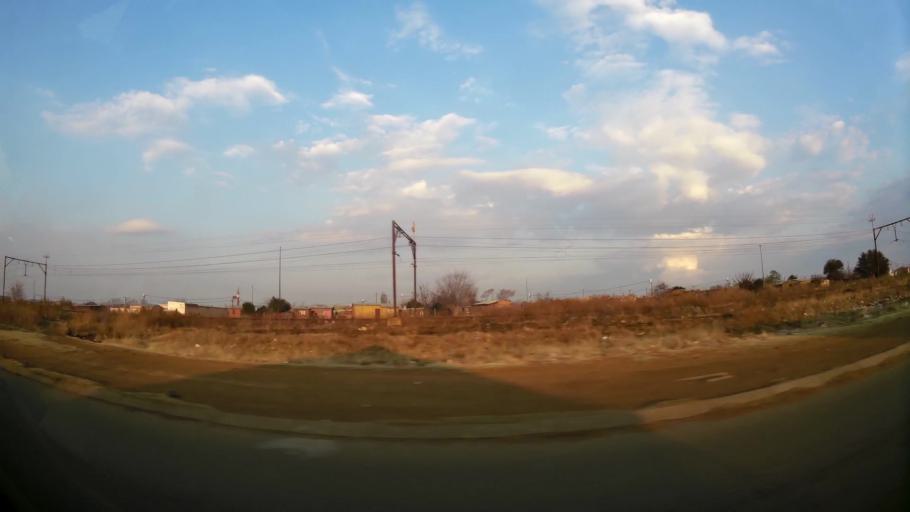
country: ZA
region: Gauteng
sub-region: City of Johannesburg Metropolitan Municipality
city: Orange Farm
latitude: -26.5498
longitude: 27.8839
